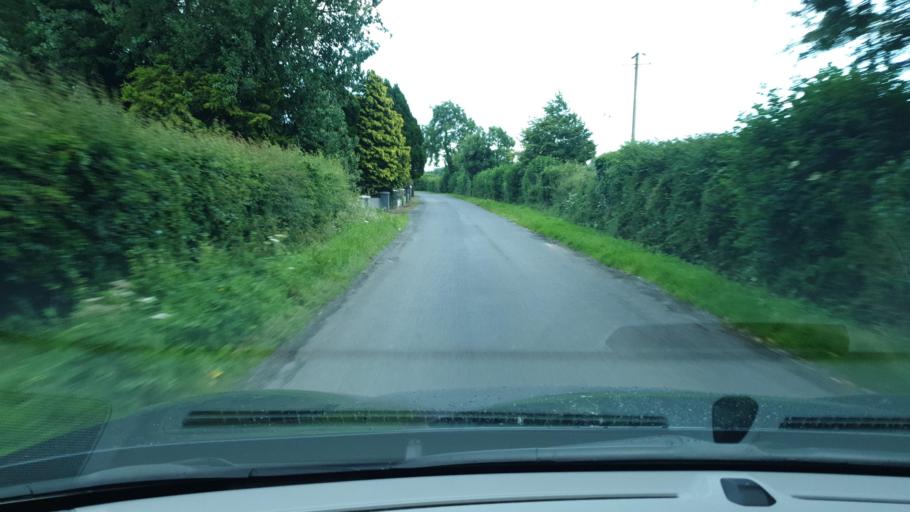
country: IE
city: Kentstown
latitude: 53.5835
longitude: -6.5548
